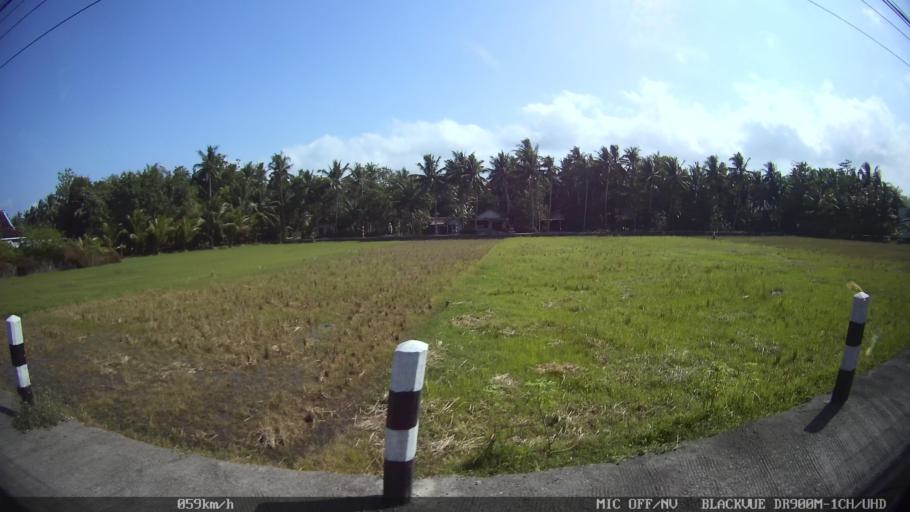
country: ID
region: Daerah Istimewa Yogyakarta
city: Srandakan
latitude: -7.9299
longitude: 110.1967
